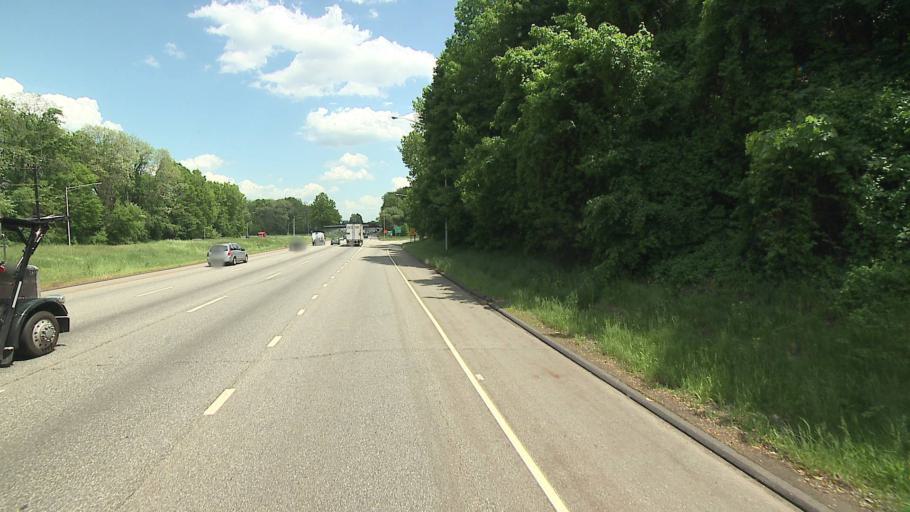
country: US
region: Connecticut
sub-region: Hartford County
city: West Hartford
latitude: 41.7498
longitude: -72.7207
